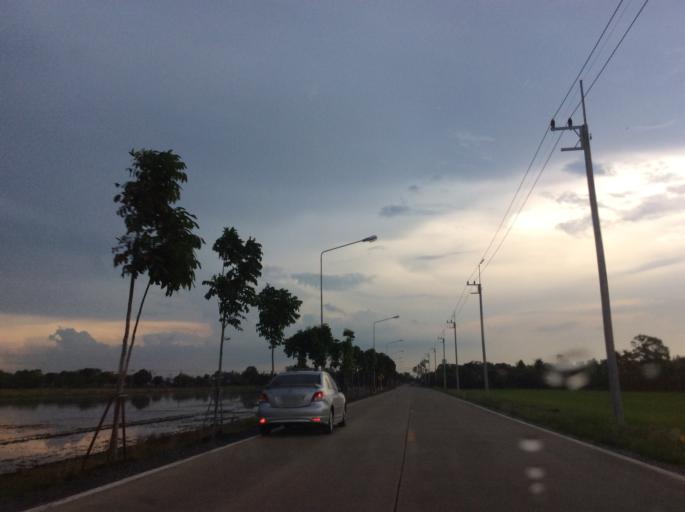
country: TH
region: Pathum Thani
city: Thanyaburi
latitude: 14.0030
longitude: 100.7345
